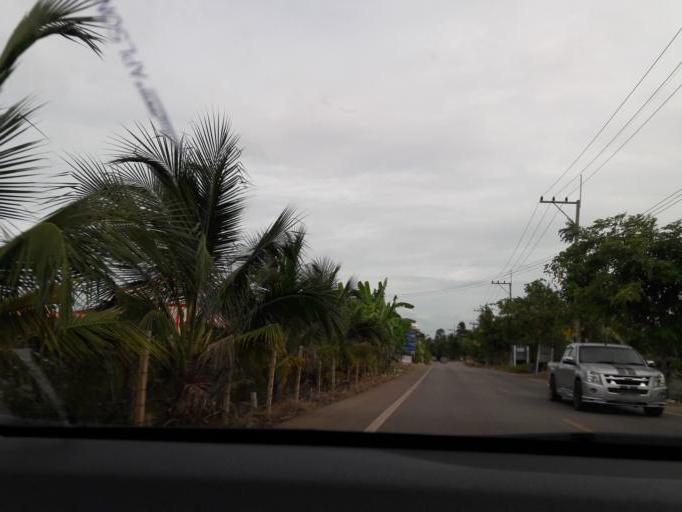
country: TH
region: Samut Sakhon
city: Ban Phaeo
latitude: 13.5619
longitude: 100.0451
